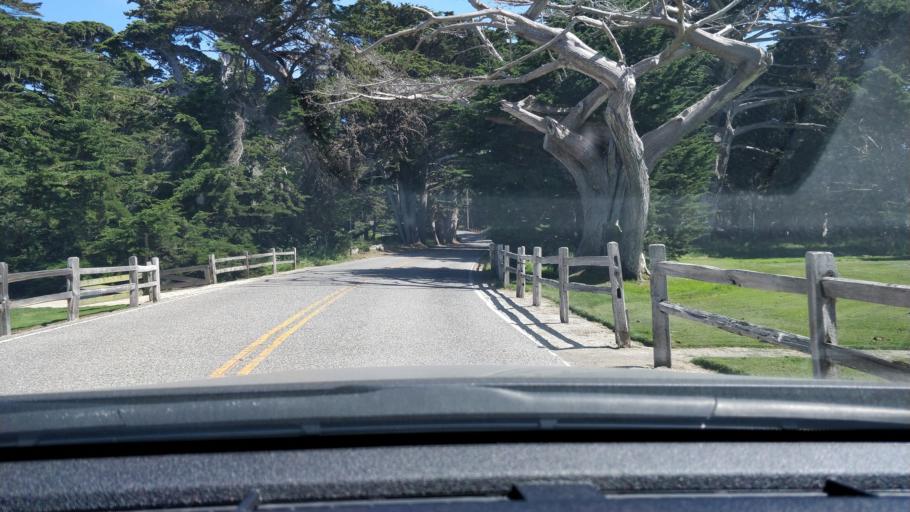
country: US
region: California
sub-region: Monterey County
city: Del Monte Forest
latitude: 36.5807
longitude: -121.9728
